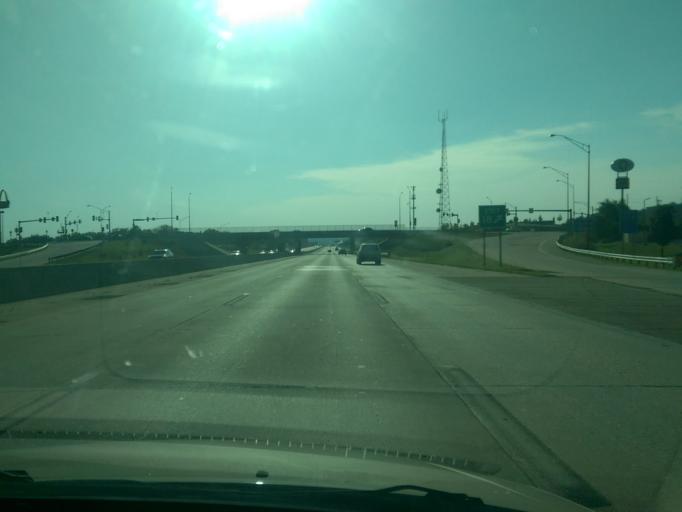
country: US
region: Missouri
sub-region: Jackson County
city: Blue Springs
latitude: 39.0341
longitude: -94.3031
